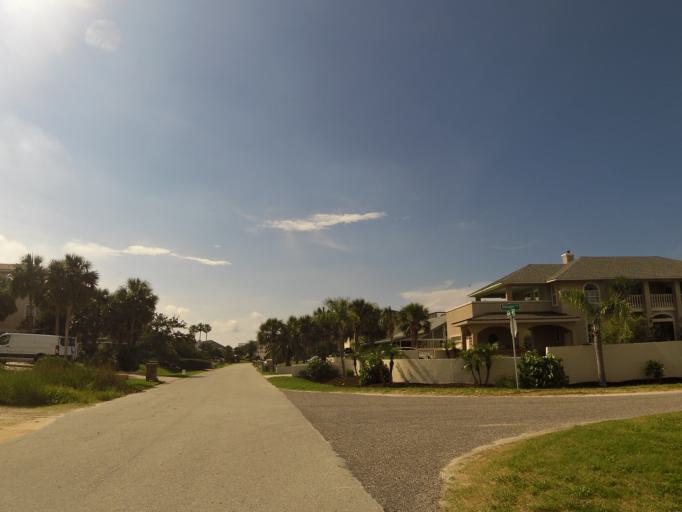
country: US
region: Florida
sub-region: Saint Johns County
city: Saint Augustine
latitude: 29.9116
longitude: -81.2955
